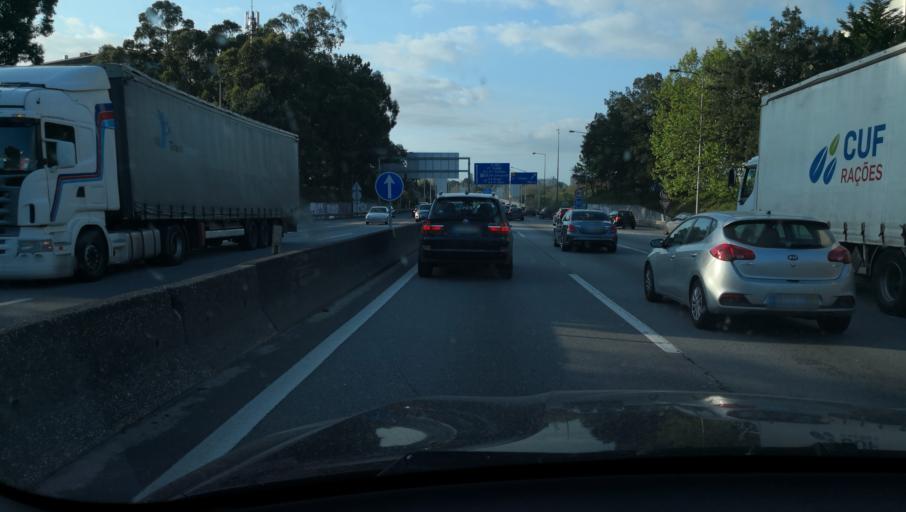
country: PT
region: Porto
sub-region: Vila Nova de Gaia
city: Canidelo
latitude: 41.1436
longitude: -8.6393
